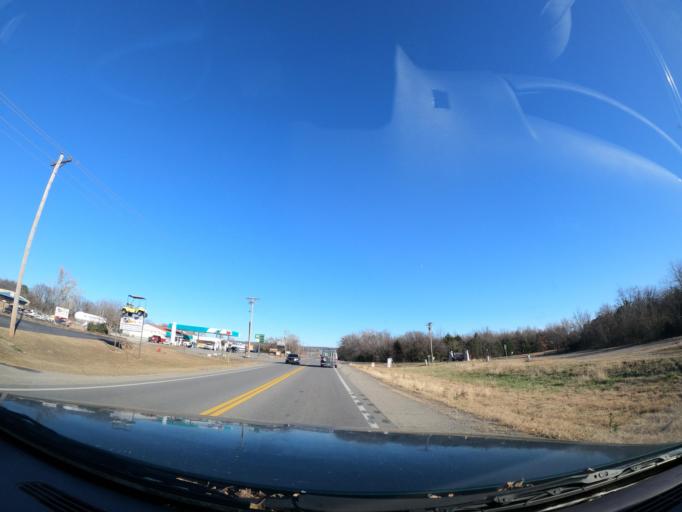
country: US
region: Oklahoma
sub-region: Pittsburg County
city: Longtown
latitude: 35.2392
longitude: -95.5135
